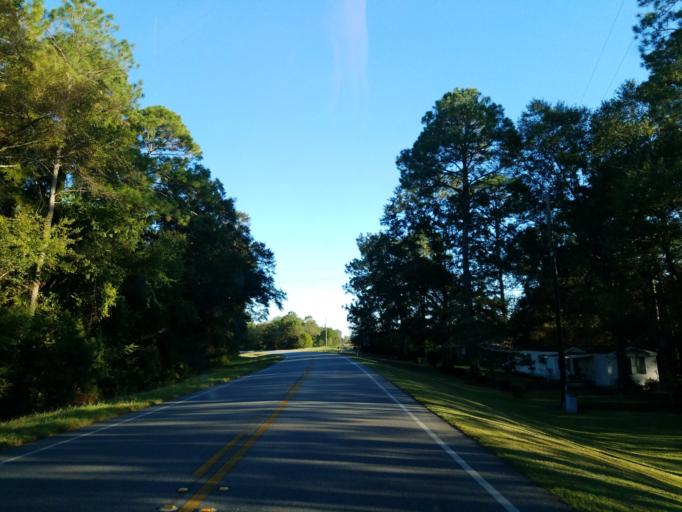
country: US
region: Georgia
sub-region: Worth County
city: Sylvester
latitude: 31.5601
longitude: -83.8491
